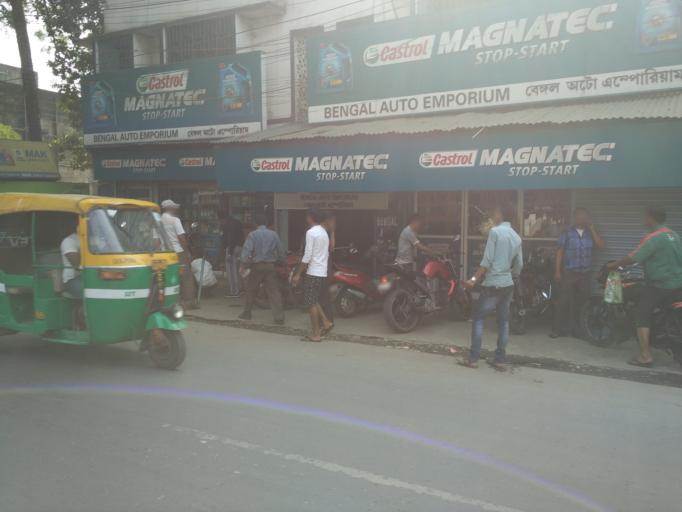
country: IN
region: West Bengal
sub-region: South 24 Paraganas
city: Baruipur
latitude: 22.4501
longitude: 88.3903
